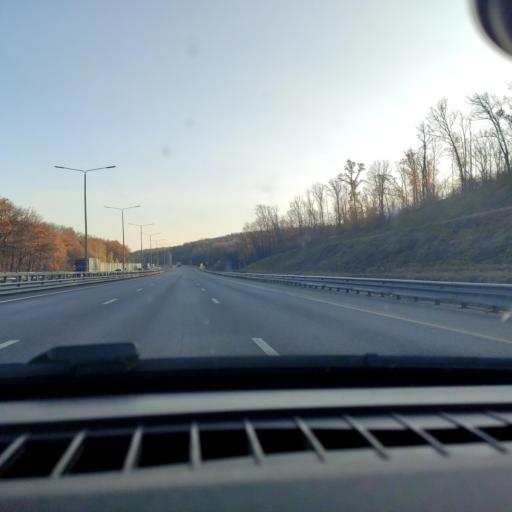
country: RU
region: Voronezj
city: Podgornoye
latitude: 51.8048
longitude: 39.2532
